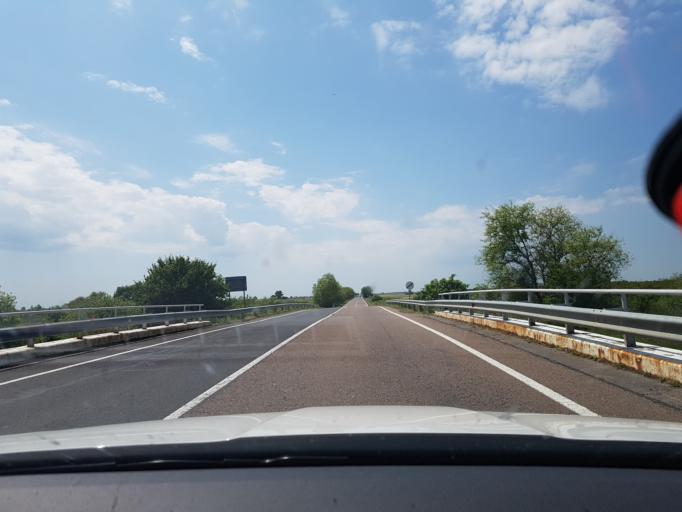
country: HU
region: Hajdu-Bihar
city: Egyek
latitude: 47.5797
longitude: 21.0002
